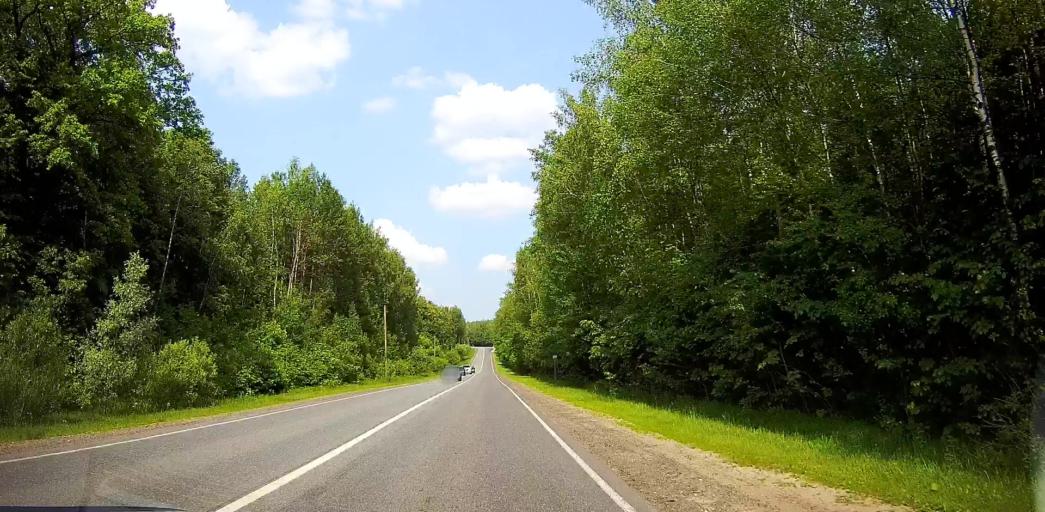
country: RU
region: Moskovskaya
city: Stupino
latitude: 54.9773
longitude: 38.1600
